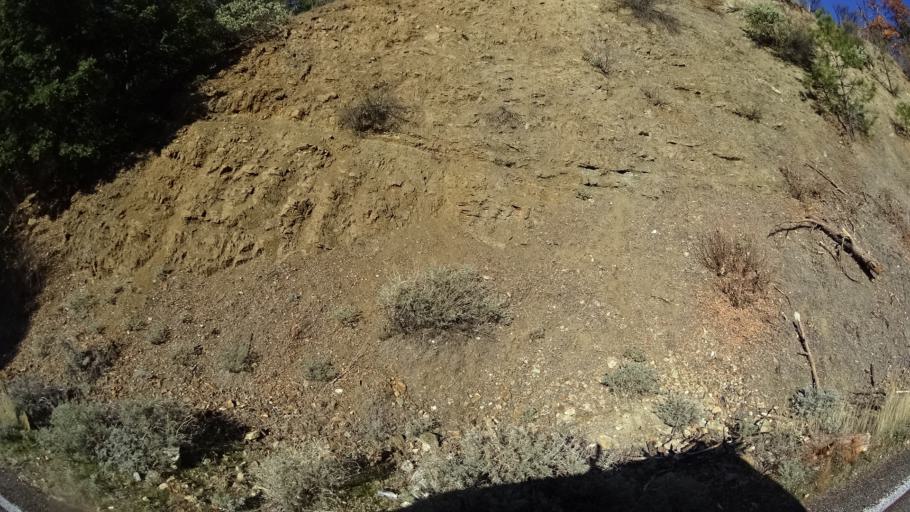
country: US
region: California
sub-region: Siskiyou County
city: Yreka
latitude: 41.8900
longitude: -122.8235
